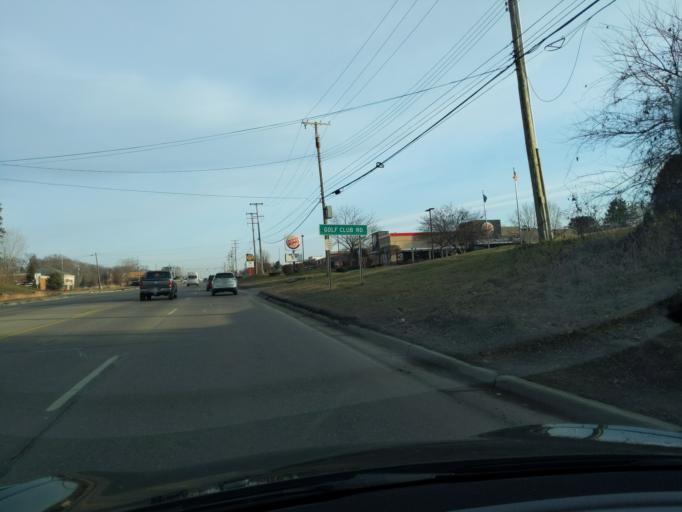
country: US
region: Michigan
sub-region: Livingston County
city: Howell
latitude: 42.6002
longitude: -83.9111
